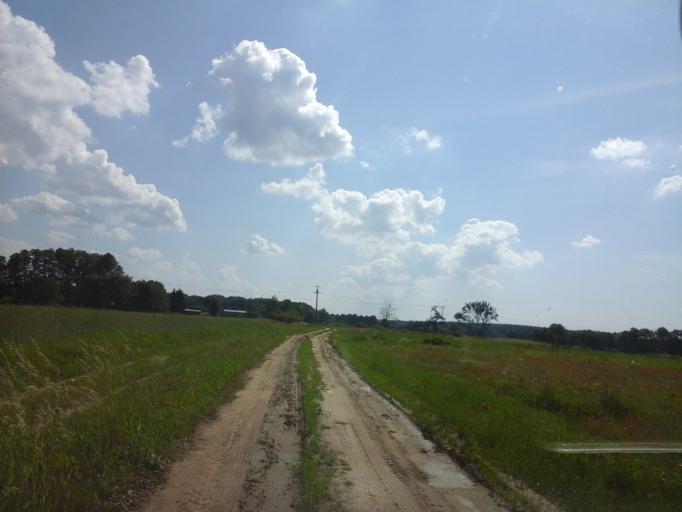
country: PL
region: Lubusz
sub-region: Powiat strzelecko-drezdenecki
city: Dobiegniew
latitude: 52.9863
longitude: 15.7443
